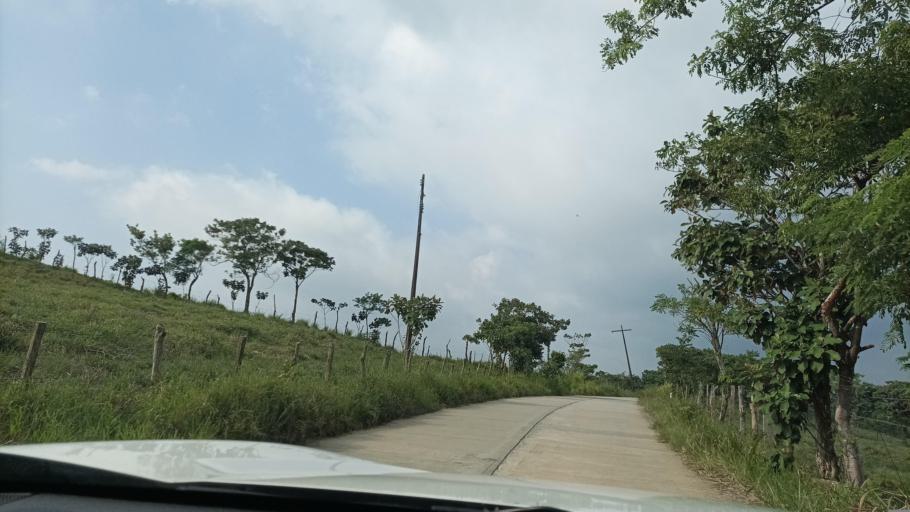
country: MX
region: Veracruz
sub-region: Moloacan
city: Tlacuilolapan
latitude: 18.0842
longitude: -94.2869
